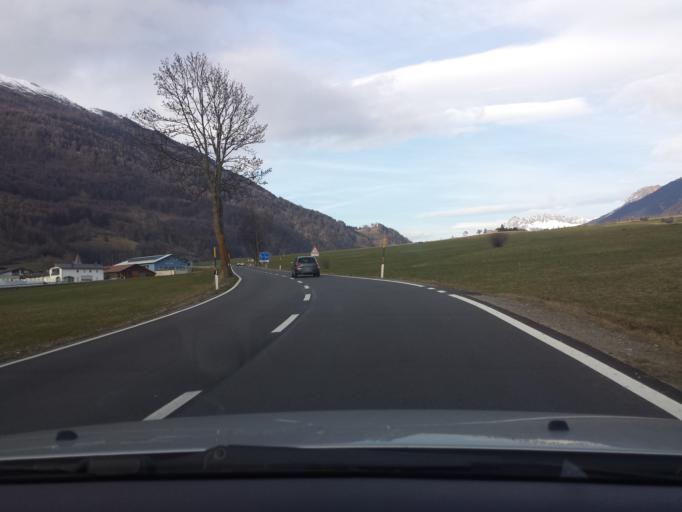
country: IT
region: Trentino-Alto Adige
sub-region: Bolzano
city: Malles Venosta
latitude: 46.7084
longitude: 10.5369
